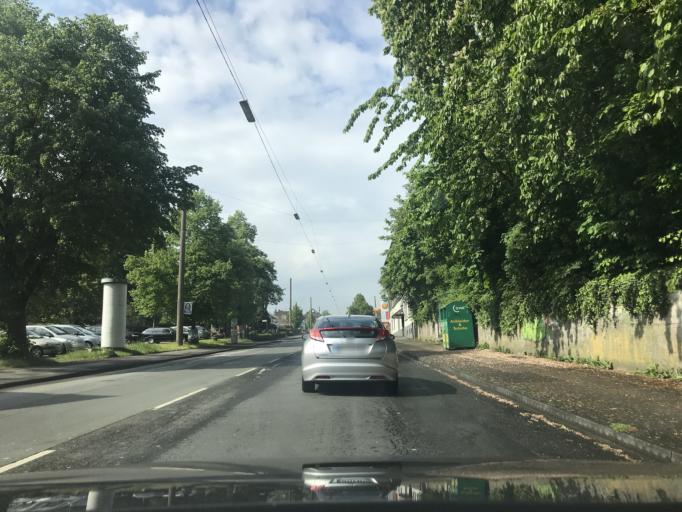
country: DE
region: North Rhine-Westphalia
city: Schwerte
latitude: 51.4490
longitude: 7.5628
